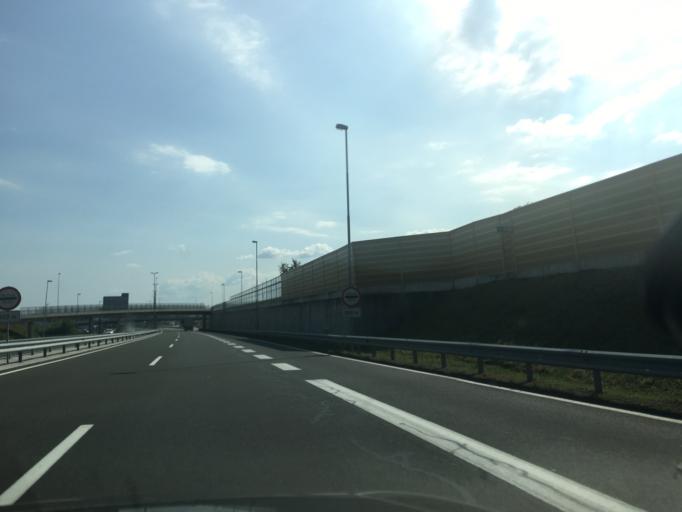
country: HR
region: Zagrebacka
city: Bregana
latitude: 45.8523
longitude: 15.6870
